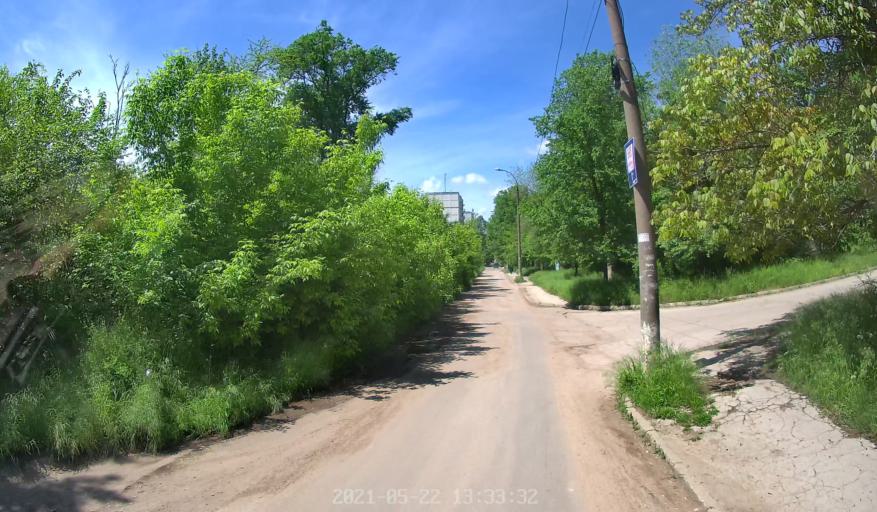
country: MD
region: Chisinau
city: Chisinau
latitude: 47.0557
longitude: 28.8201
